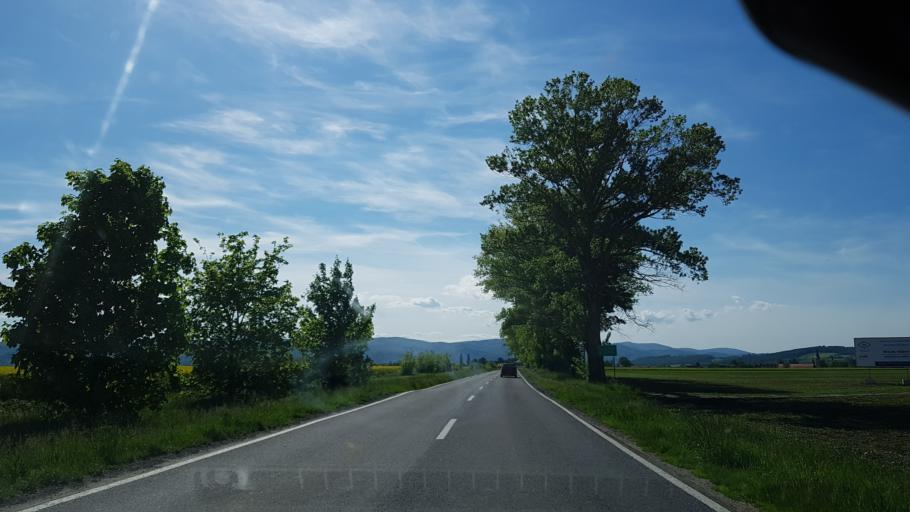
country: PL
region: Lower Silesian Voivodeship
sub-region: Powiat zabkowicki
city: Stoszowice
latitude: 50.5981
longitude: 16.7667
